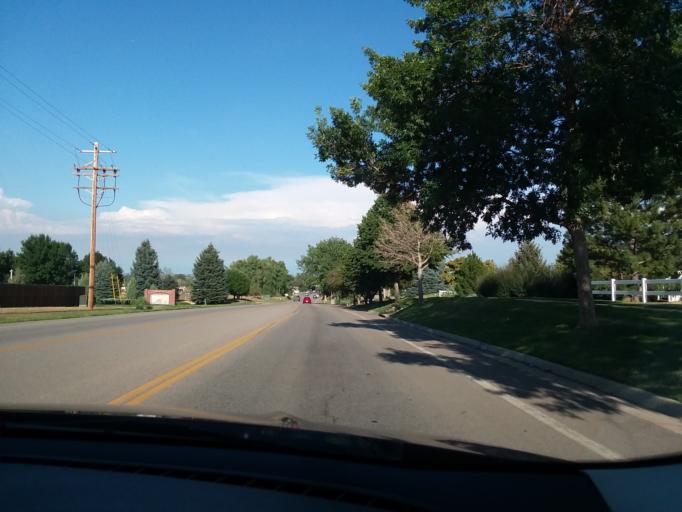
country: US
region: Colorado
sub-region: Larimer County
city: Fort Collins
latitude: 40.4947
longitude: -105.0834
